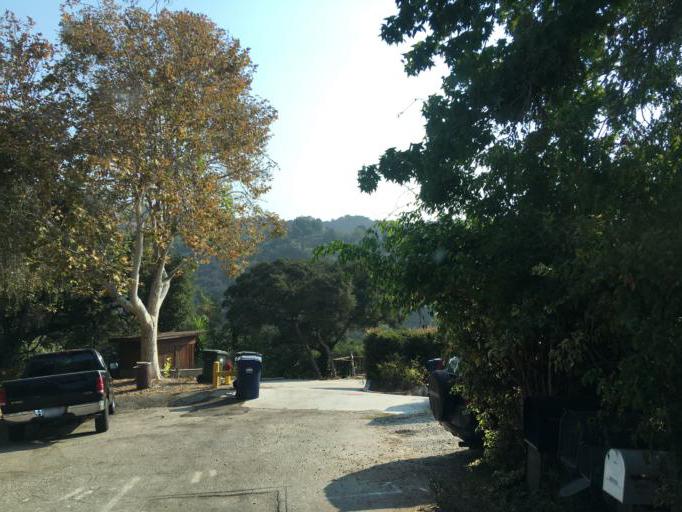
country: US
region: California
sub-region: Los Angeles County
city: Topanga
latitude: 34.0805
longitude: -118.6006
